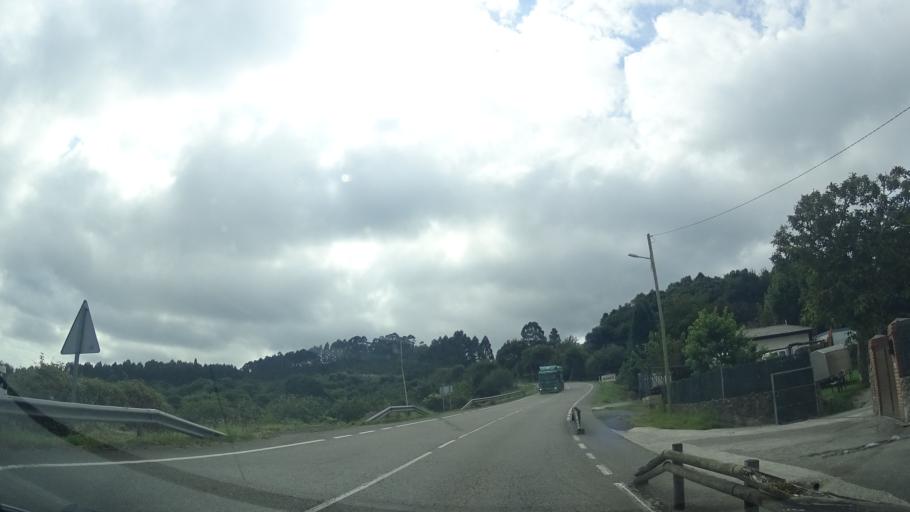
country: ES
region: Asturias
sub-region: Province of Asturias
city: Ribadesella
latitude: 43.4616
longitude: -5.1207
